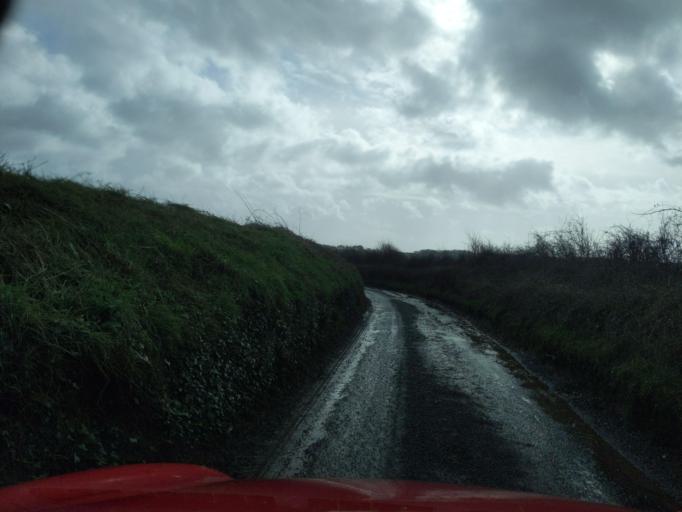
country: GB
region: England
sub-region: Devon
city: Ivybridge
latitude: 50.3569
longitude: -3.9295
